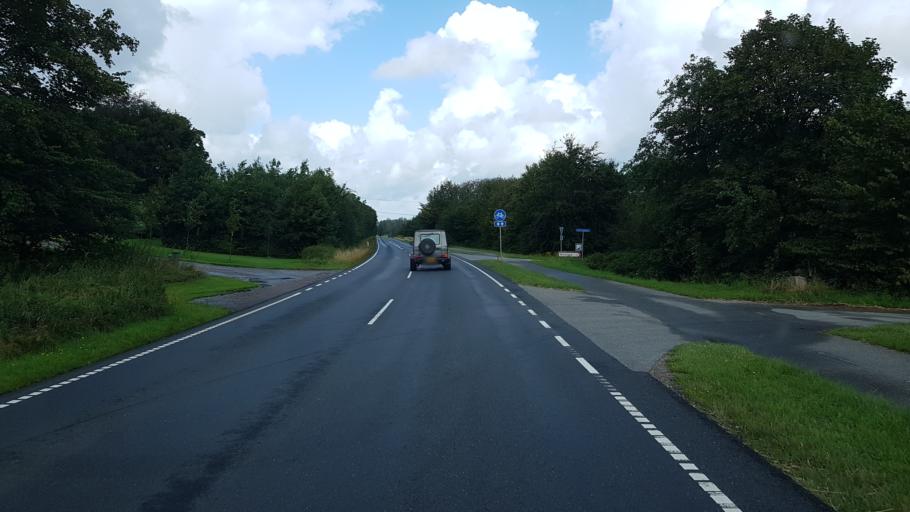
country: DK
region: South Denmark
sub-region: Vejen Kommune
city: Vejen
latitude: 55.5077
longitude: 9.1314
